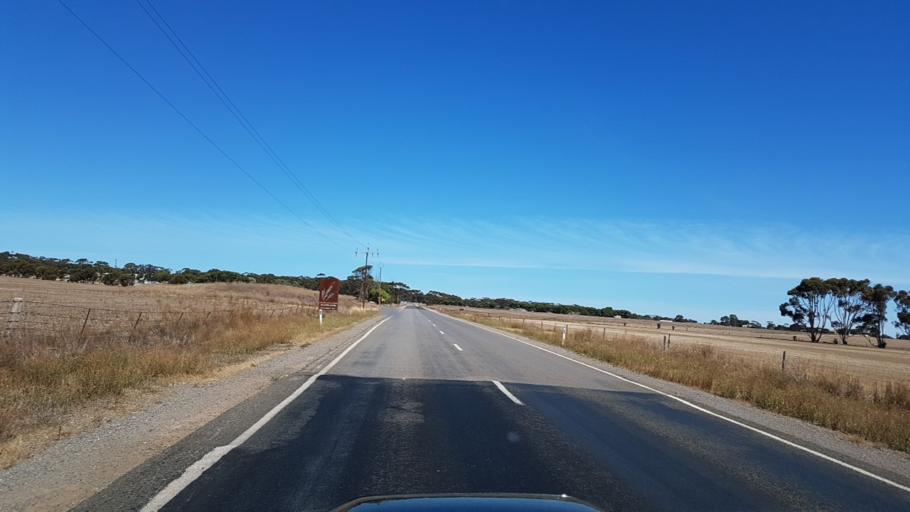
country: AU
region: South Australia
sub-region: Yorke Peninsula
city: Maitland
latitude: -34.3616
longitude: 137.6670
